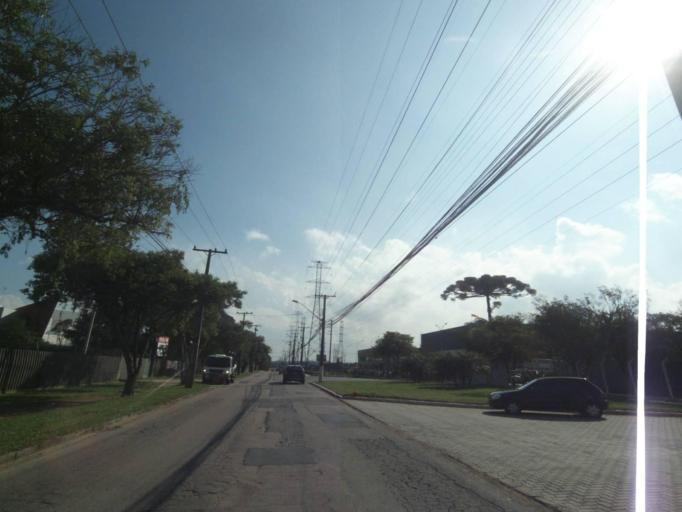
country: BR
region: Parana
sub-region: Araucaria
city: Araucaria
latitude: -25.5311
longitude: -49.3286
